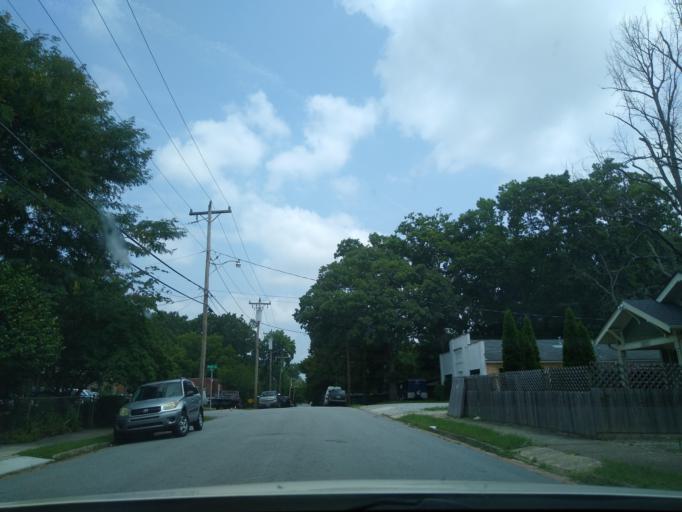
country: US
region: North Carolina
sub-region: Guilford County
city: Greensboro
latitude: 36.0530
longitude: -79.8099
